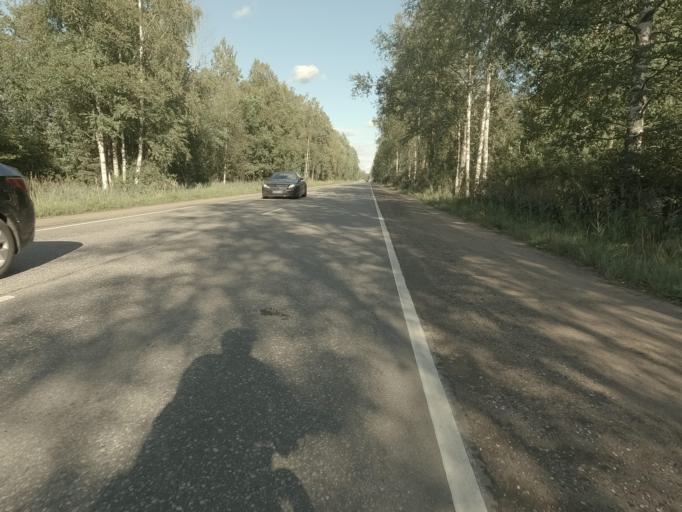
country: RU
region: Leningrad
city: Imeni Morozova
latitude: 59.9740
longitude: 30.9958
